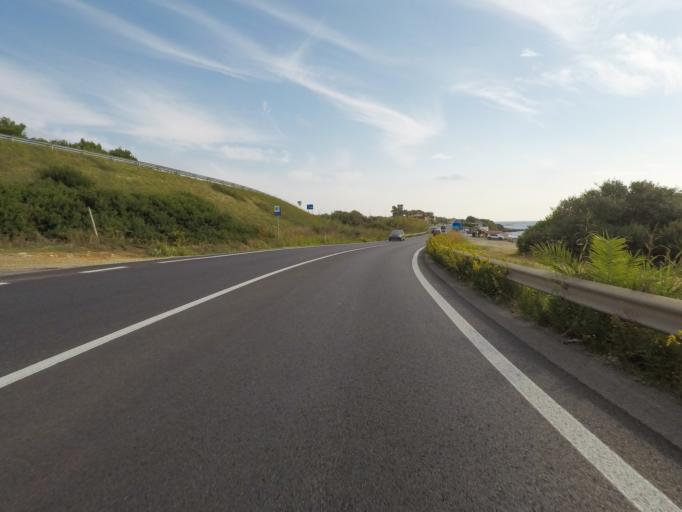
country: IT
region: Latium
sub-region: Citta metropolitana di Roma Capitale
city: Civitavecchia
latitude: 42.0570
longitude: 11.8195
